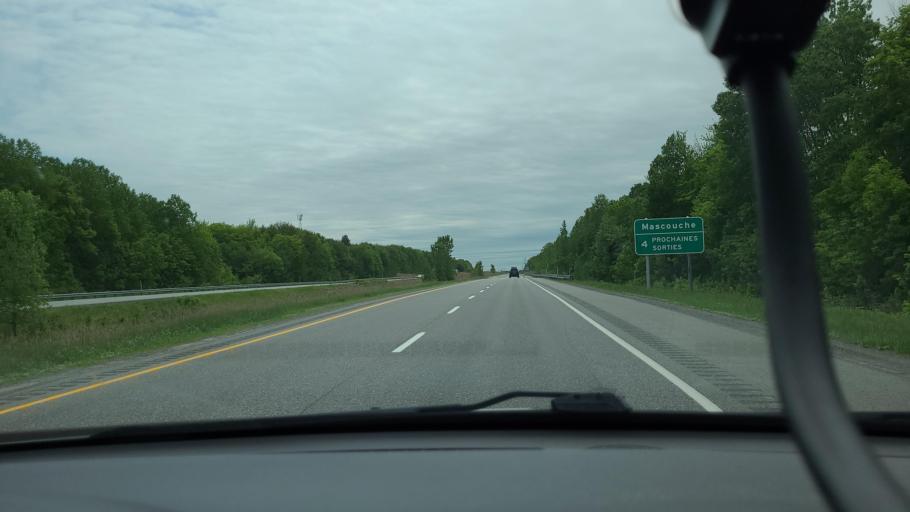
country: CA
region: Quebec
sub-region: Lanaudiere
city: Mascouche
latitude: 45.8088
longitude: -73.5924
